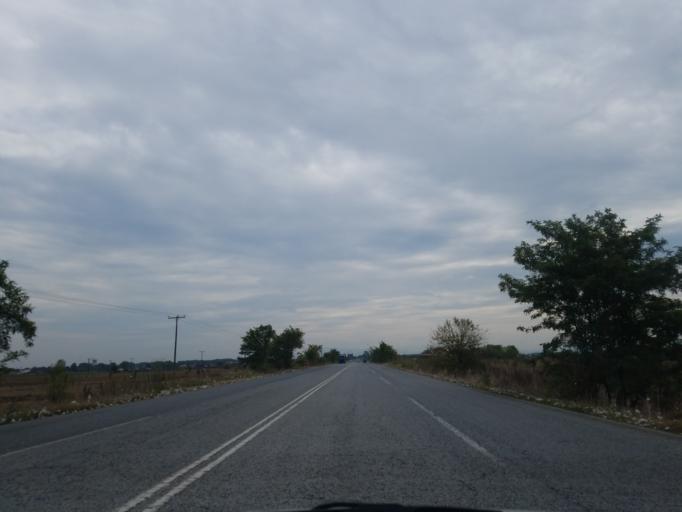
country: GR
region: Thessaly
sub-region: Nomos Kardhitsas
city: Sofades
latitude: 39.3480
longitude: 22.0707
